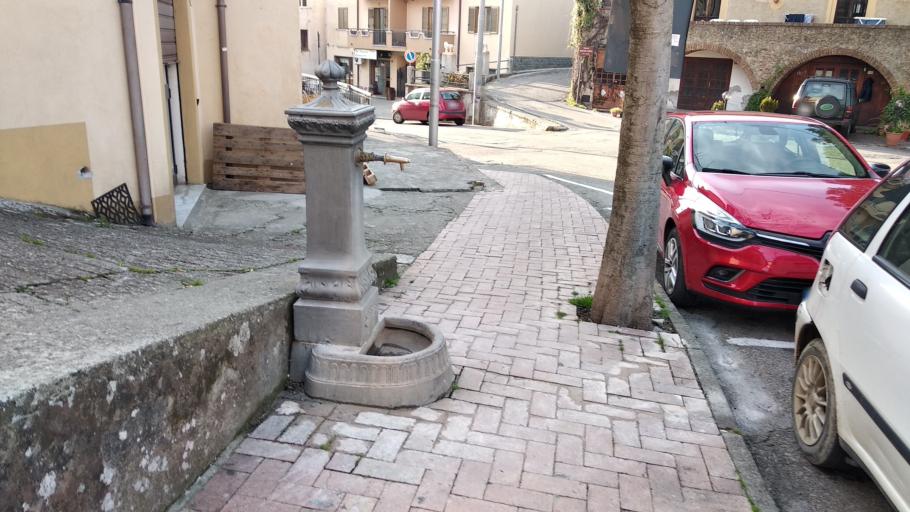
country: IT
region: Calabria
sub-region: Provincia di Cosenza
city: San Marco Argentano
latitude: 39.5566
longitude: 16.1229
